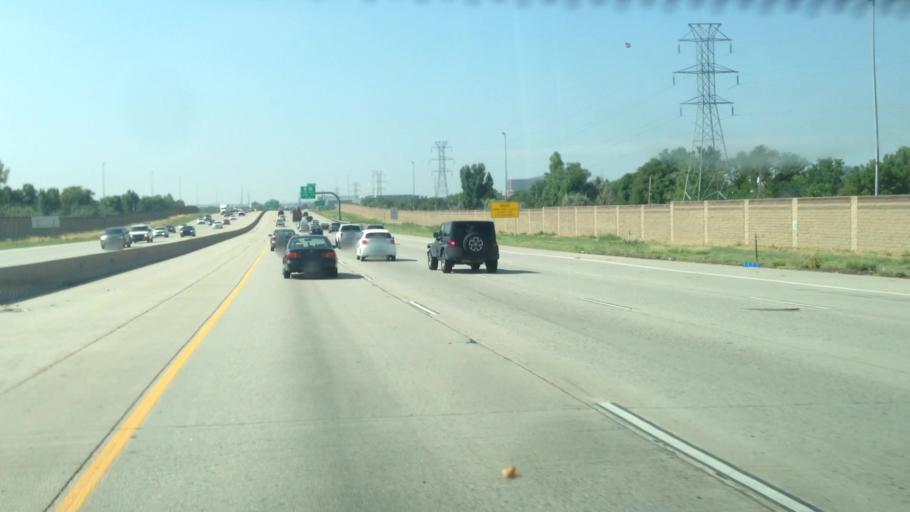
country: US
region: Colorado
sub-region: Adams County
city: Aurora
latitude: 39.7620
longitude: -104.8277
